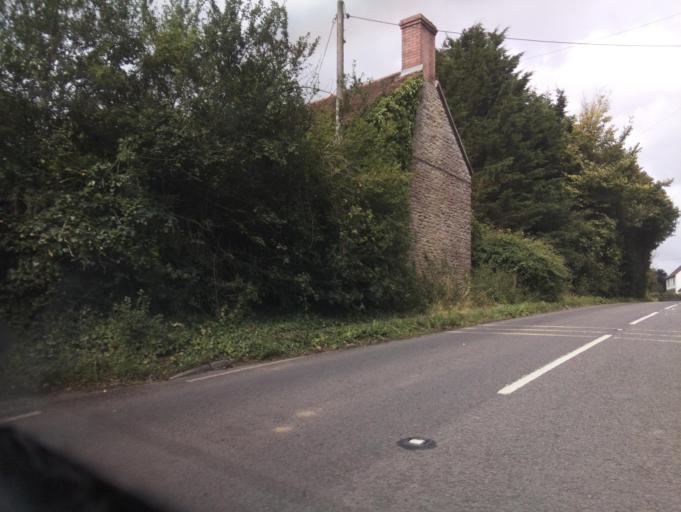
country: GB
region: England
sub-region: Dorset
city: Stalbridge
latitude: 50.9958
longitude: -2.4136
